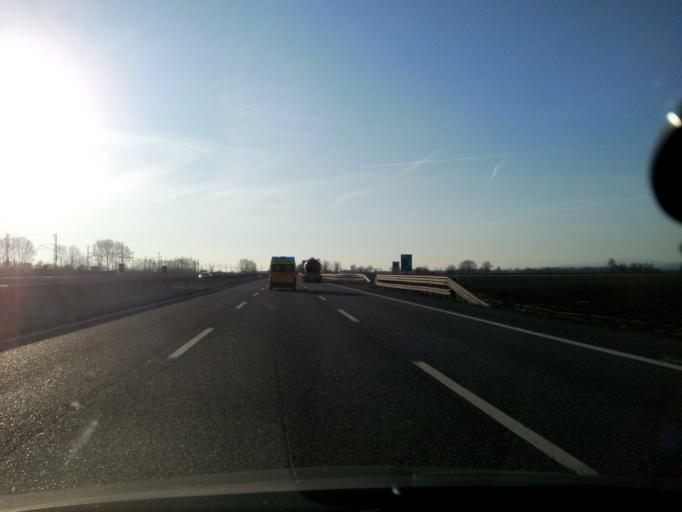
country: IT
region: Emilia-Romagna
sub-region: Provincia di Piacenza
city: Alseno
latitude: 44.9279
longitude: 9.9834
